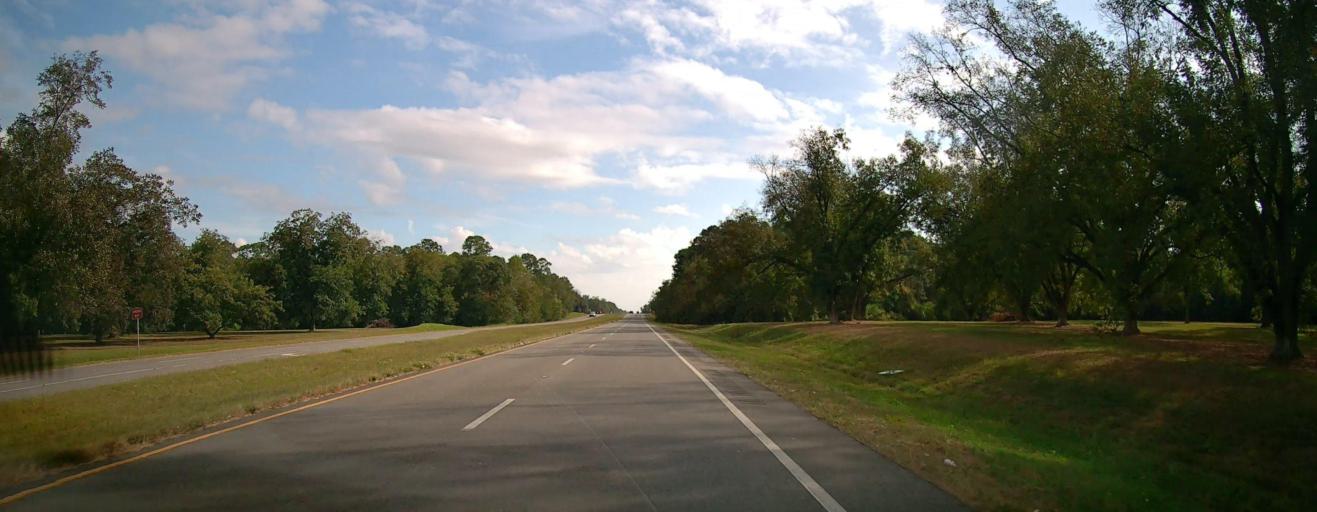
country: US
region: Georgia
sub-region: Thomas County
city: Meigs
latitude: 31.0136
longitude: -84.0545
